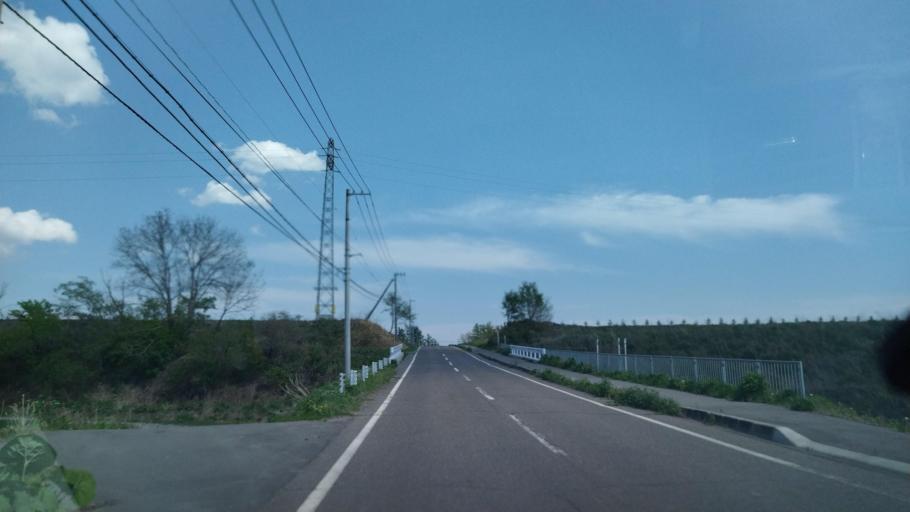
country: JP
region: Hokkaido
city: Otofuke
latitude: 43.1009
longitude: 143.2200
